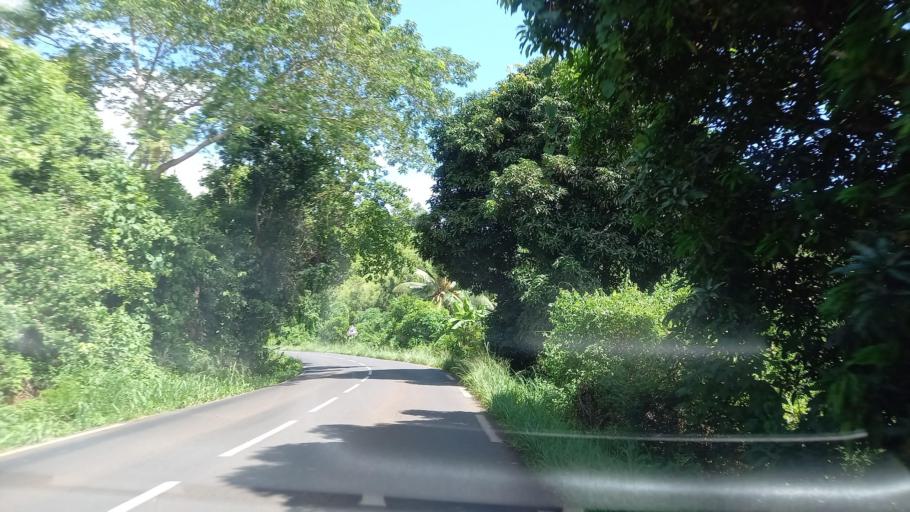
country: YT
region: Bandraboua
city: Bandraboua
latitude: -12.7164
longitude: 45.1289
